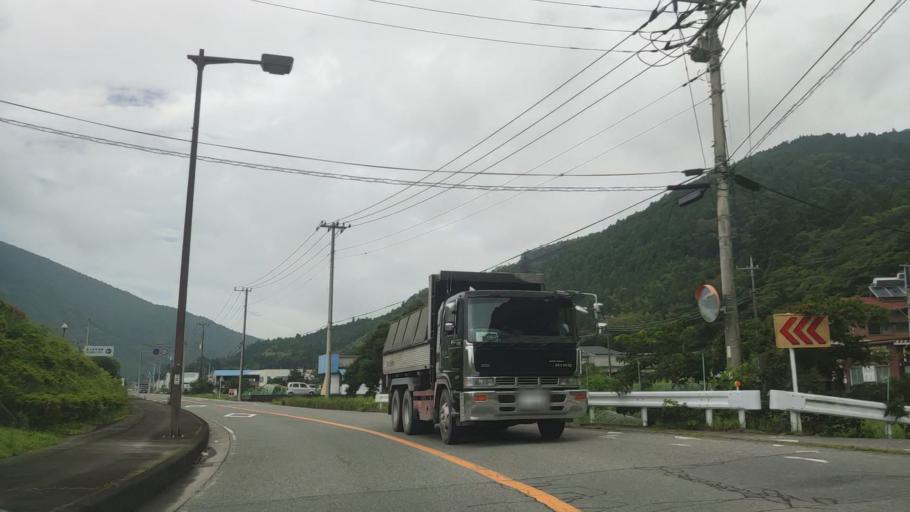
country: JP
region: Shizuoka
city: Fujinomiya
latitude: 35.2083
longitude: 138.5533
